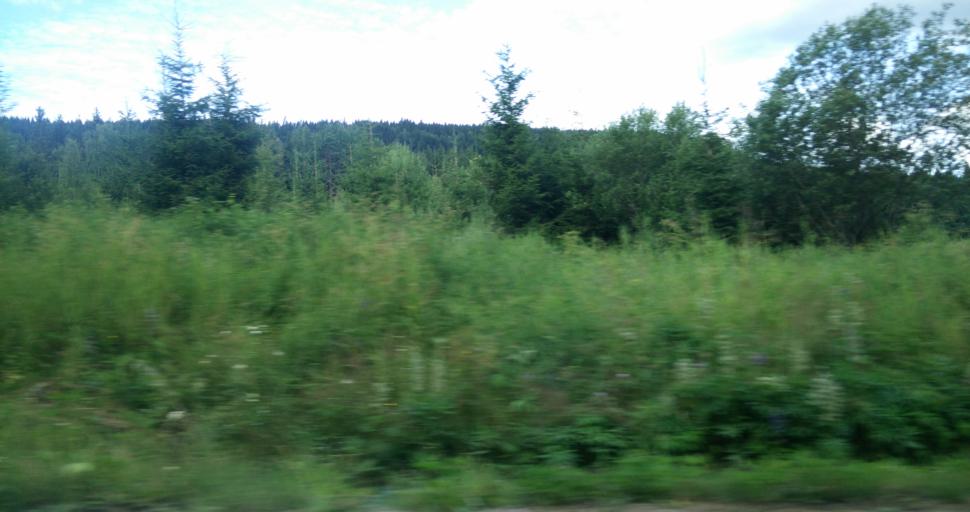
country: SE
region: Vaermland
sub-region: Hagfors Kommun
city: Ekshaerad
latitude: 60.0598
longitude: 13.4790
